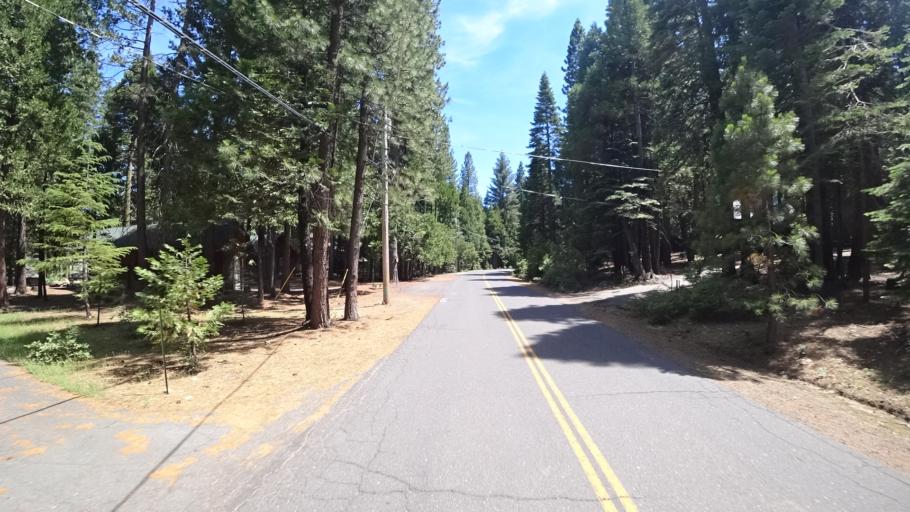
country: US
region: California
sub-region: Calaveras County
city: Arnold
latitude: 38.3091
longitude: -120.2612
